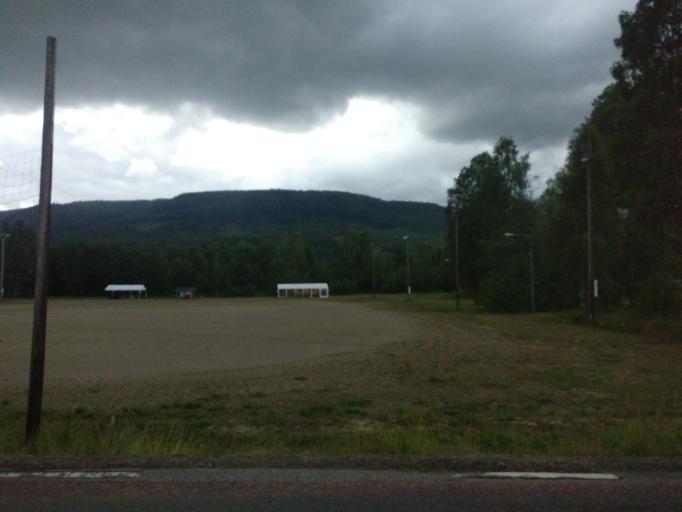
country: SE
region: Vaermland
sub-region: Torsby Kommun
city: Torsby
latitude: 60.7366
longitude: 12.8634
